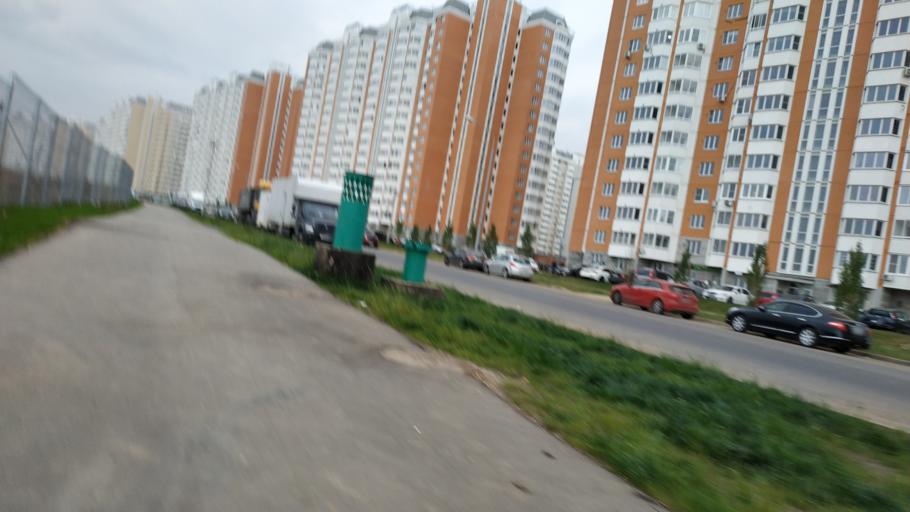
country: RU
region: Moscow
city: Novo-Peredelkino
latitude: 55.6375
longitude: 37.3131
